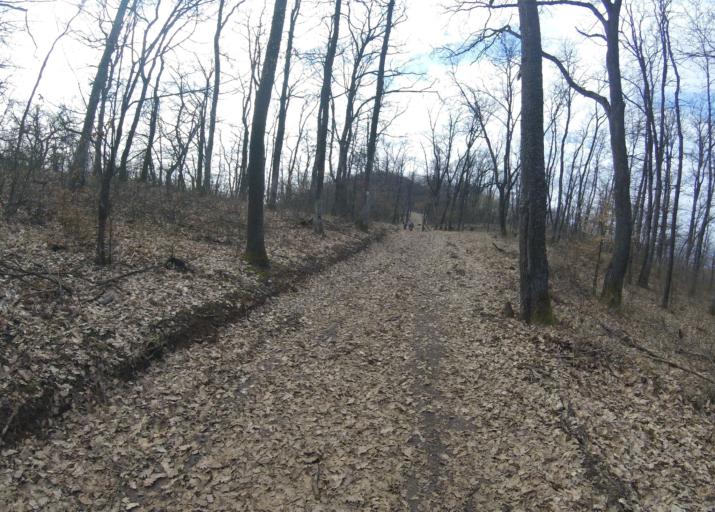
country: HU
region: Heves
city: Belapatfalva
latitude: 48.0113
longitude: 20.3426
